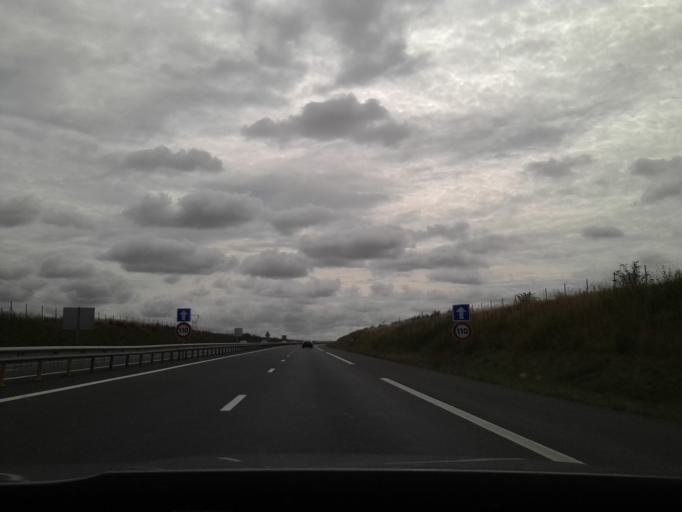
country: FR
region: Lower Normandy
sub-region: Departement du Calvados
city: Fleury-sur-Orne
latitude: 49.1331
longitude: -0.3756
